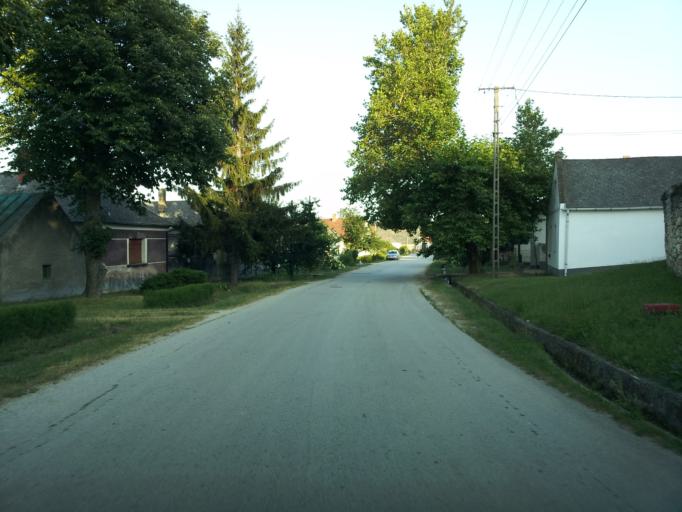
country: HU
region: Veszprem
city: Ajka
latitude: 46.9790
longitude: 17.5692
